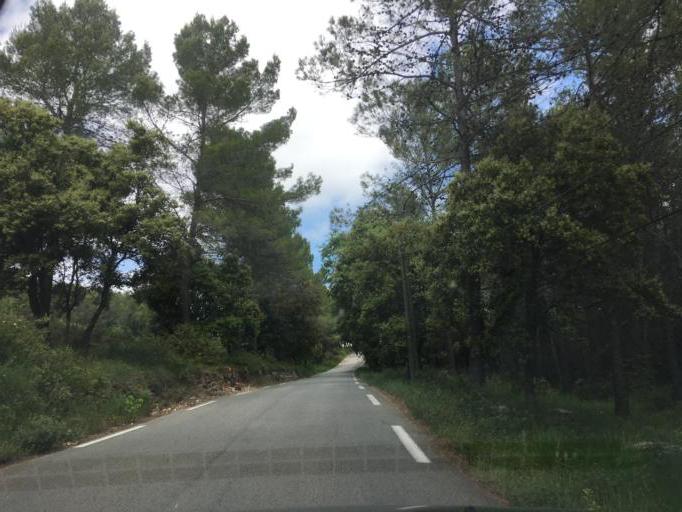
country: FR
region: Provence-Alpes-Cote d'Azur
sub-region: Departement du Var
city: Taradeau
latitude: 43.4714
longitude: 6.4318
